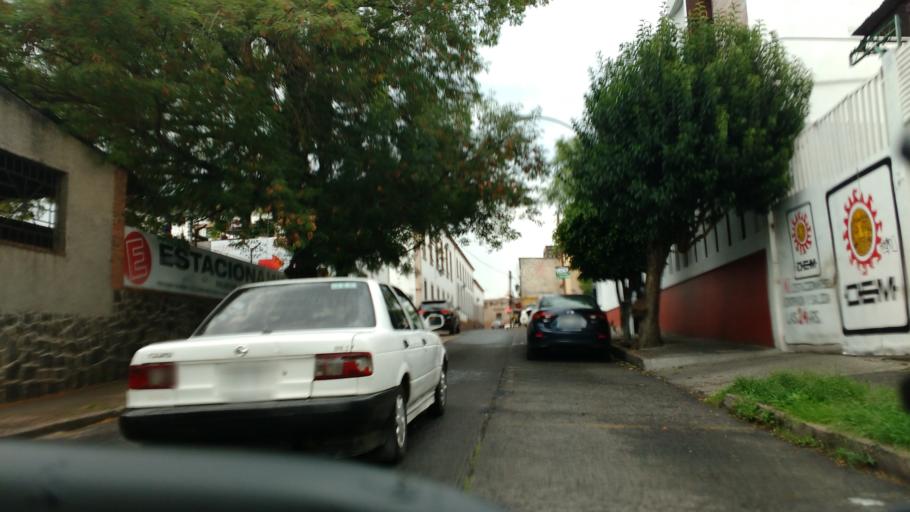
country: MX
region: Michoacan
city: Morelia
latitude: 19.7016
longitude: -101.1839
